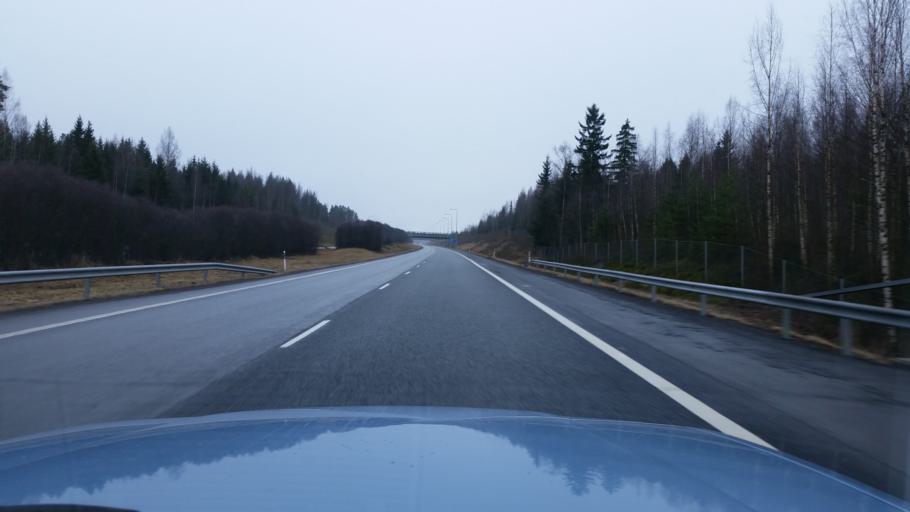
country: FI
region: Pirkanmaa
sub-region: Etelae-Pirkanmaa
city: Toijala
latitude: 61.2328
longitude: 23.8369
